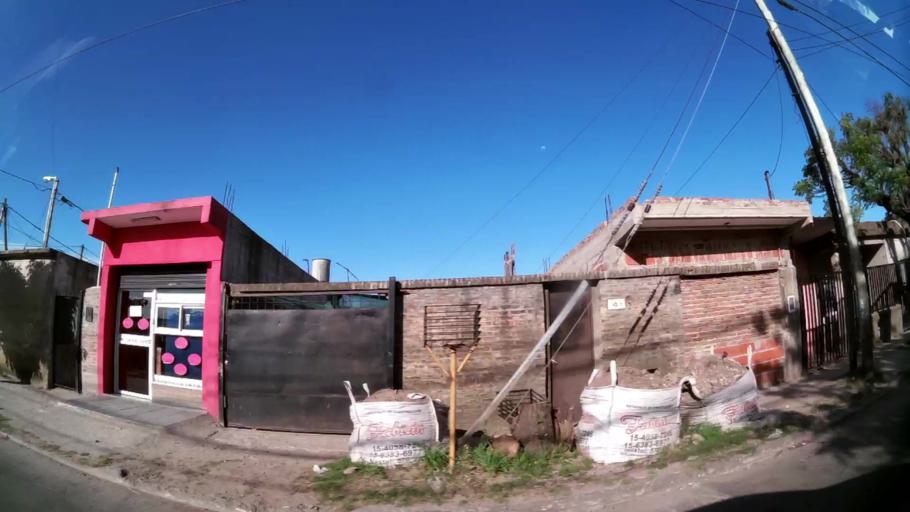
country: AR
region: Buenos Aires
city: Santa Catalina - Dique Lujan
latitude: -34.4999
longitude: -58.7272
